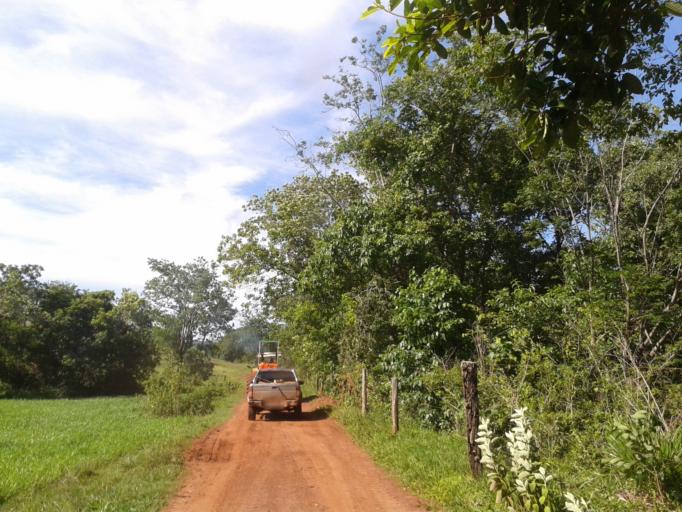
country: BR
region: Minas Gerais
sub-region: Santa Vitoria
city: Santa Vitoria
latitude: -19.0777
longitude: -50.0145
